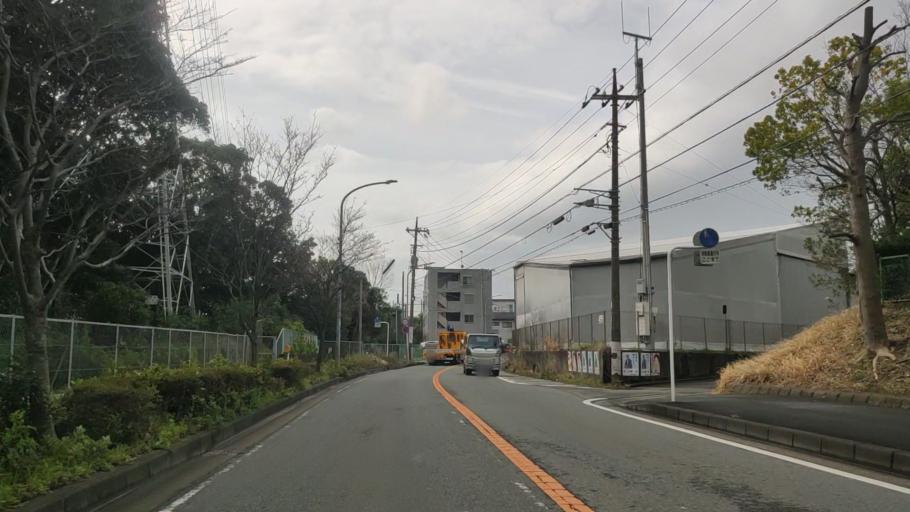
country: JP
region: Kanagawa
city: Fujisawa
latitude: 35.3738
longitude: 139.5242
